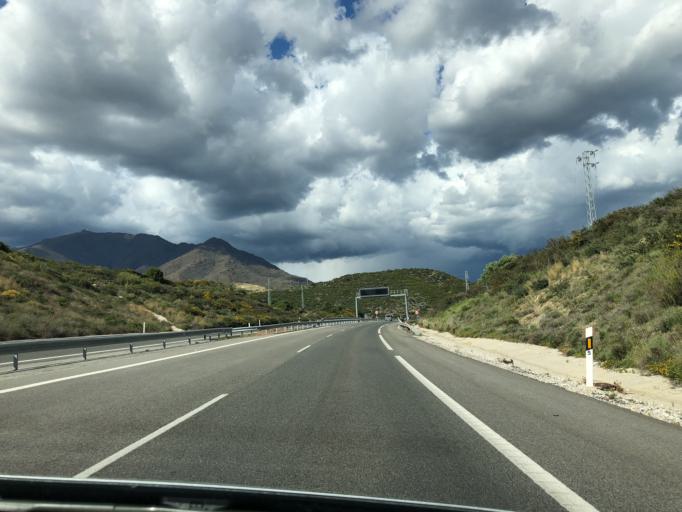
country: ES
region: Andalusia
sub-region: Provincia de Malaga
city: Manilva
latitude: 36.4194
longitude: -5.2194
